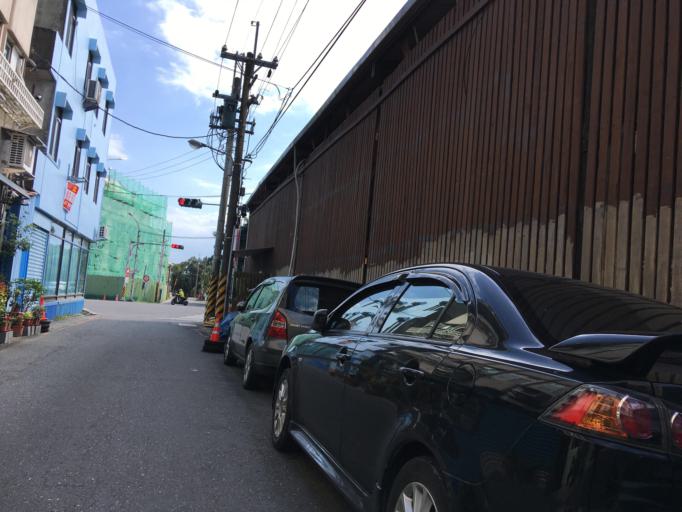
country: TW
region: Taiwan
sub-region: Yilan
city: Yilan
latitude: 24.8370
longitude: 121.7856
